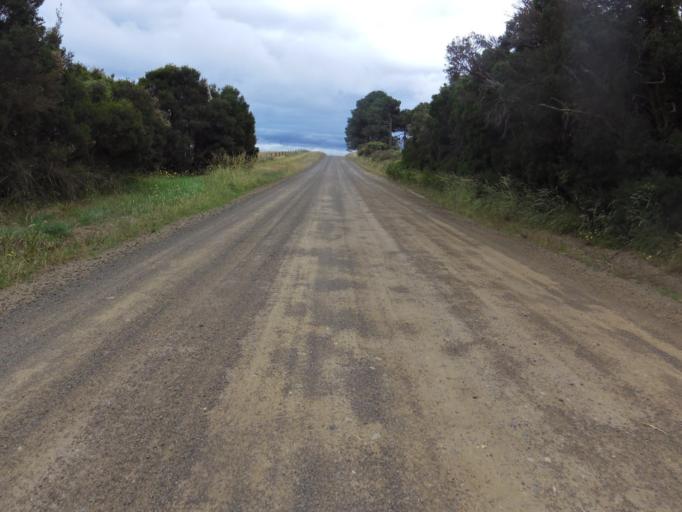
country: AU
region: Victoria
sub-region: Bass Coast
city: Cowes
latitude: -38.3841
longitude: 145.3503
